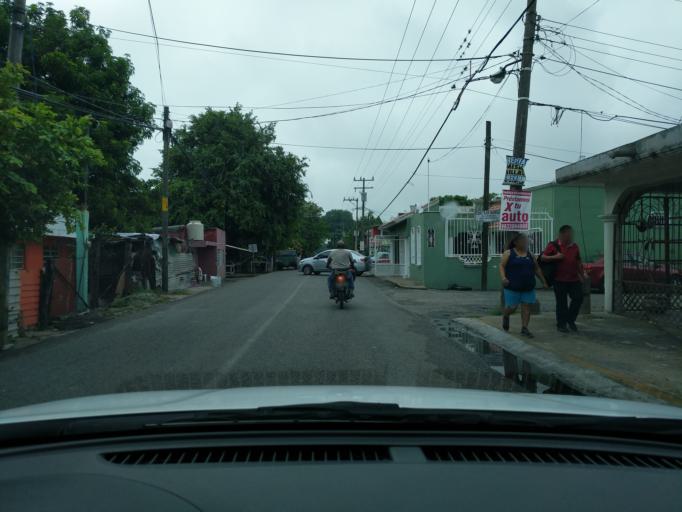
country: MX
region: Tabasco
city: Villahermosa
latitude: 17.9549
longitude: -92.9650
